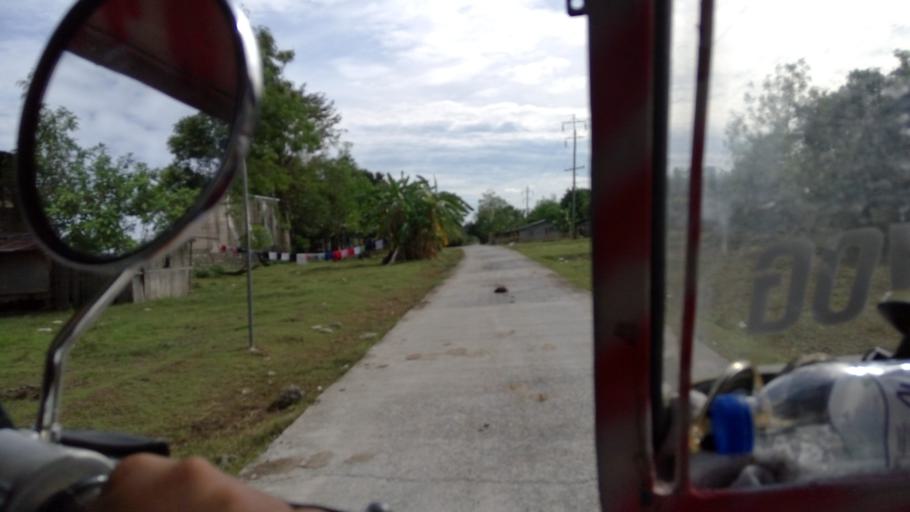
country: PH
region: Ilocos
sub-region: Province of La Union
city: San Eugenio
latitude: 16.3756
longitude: 120.3523
